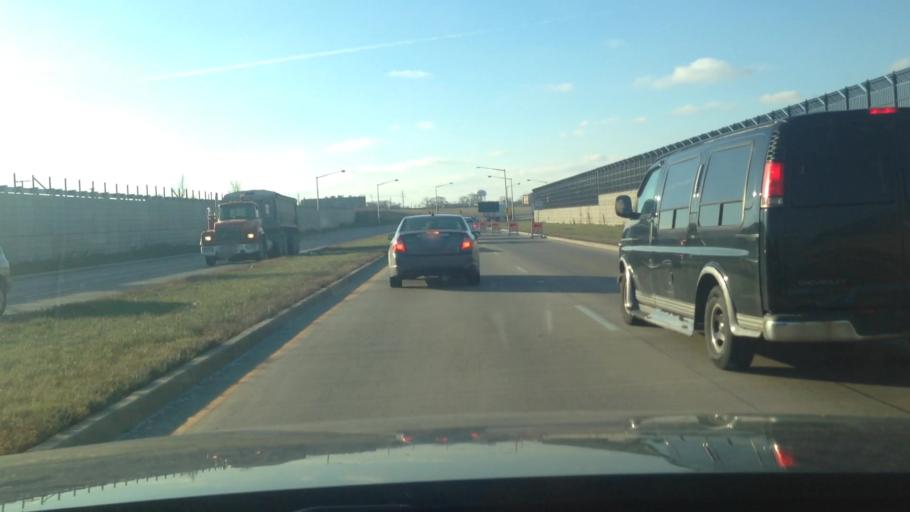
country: US
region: Illinois
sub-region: DuPage County
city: Bensenville
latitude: 41.9557
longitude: -87.9300
